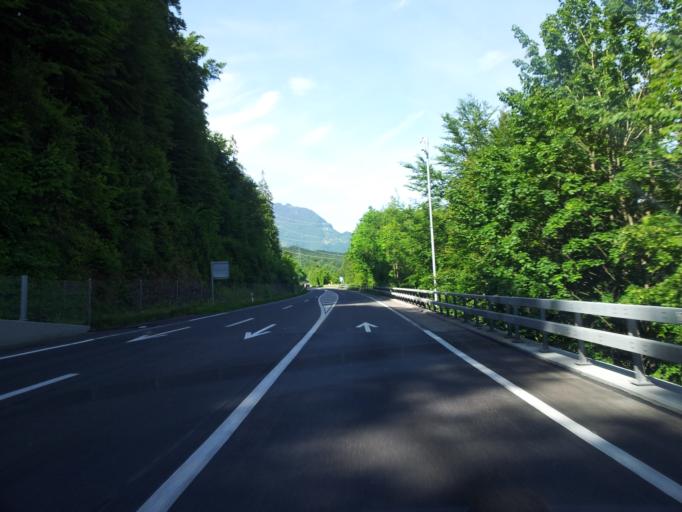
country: CH
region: Bern
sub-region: Interlaken-Oberhasli District
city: Ringgenberg
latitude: 46.6928
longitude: 7.9306
